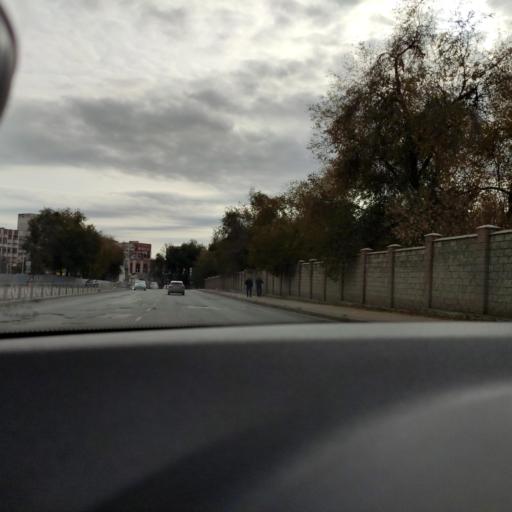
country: RU
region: Samara
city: Petra-Dubrava
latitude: 53.2423
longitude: 50.2728
